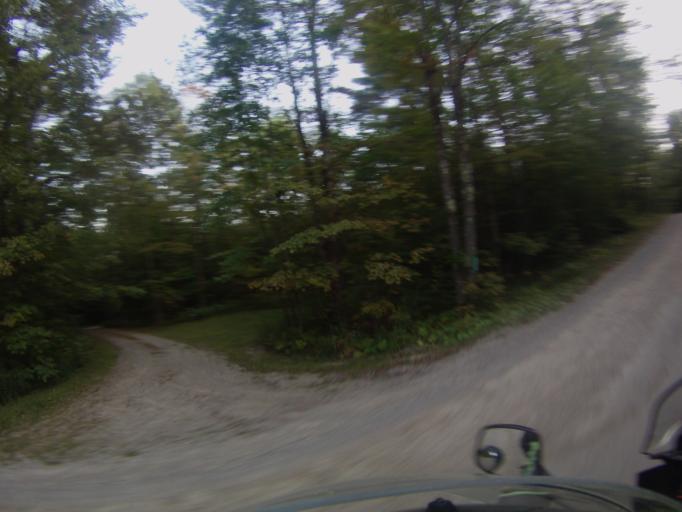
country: US
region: Vermont
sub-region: Addison County
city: Bristol
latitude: 44.0126
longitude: -73.0297
